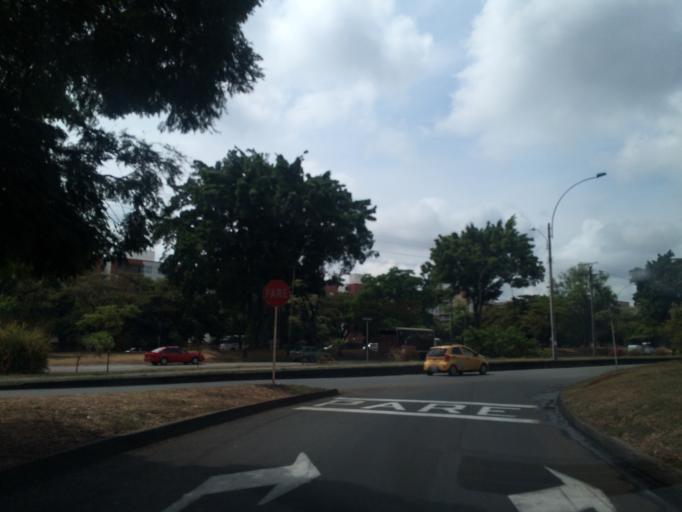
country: CO
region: Valle del Cauca
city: Cali
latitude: 3.3793
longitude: -76.5255
